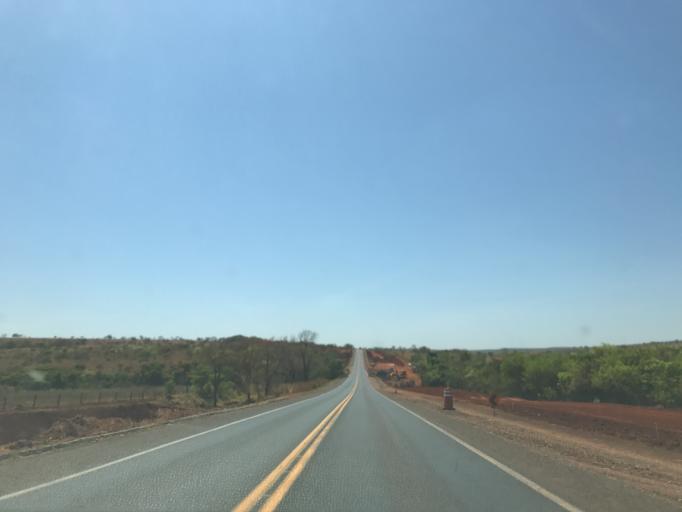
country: BR
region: Minas Gerais
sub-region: Prata
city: Prata
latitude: -19.4392
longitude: -48.8889
